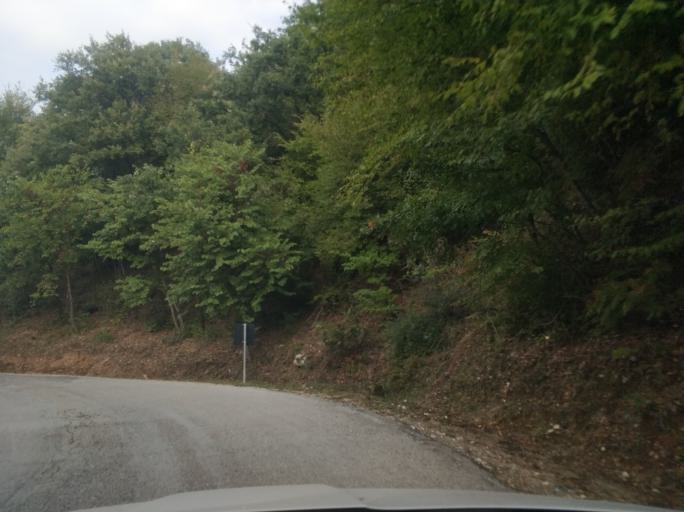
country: AL
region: Vlore
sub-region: Rrethi i Sarandes
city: Dhiver
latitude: 39.9201
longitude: 20.2009
